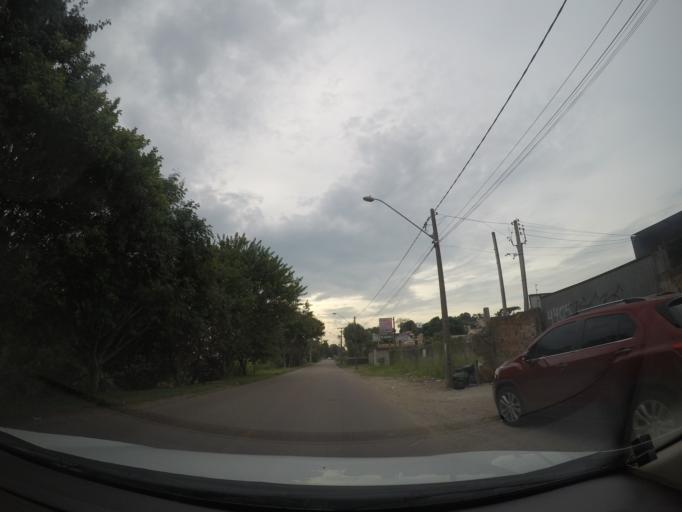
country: BR
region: Parana
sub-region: Curitiba
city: Curitiba
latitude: -25.4691
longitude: -49.2475
